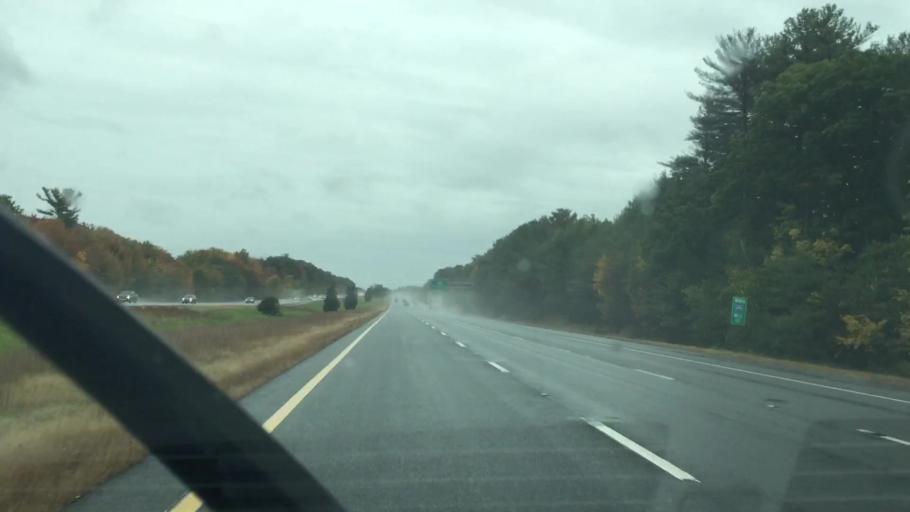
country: US
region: Massachusetts
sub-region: Essex County
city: Amesbury
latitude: 42.8353
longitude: -70.9583
